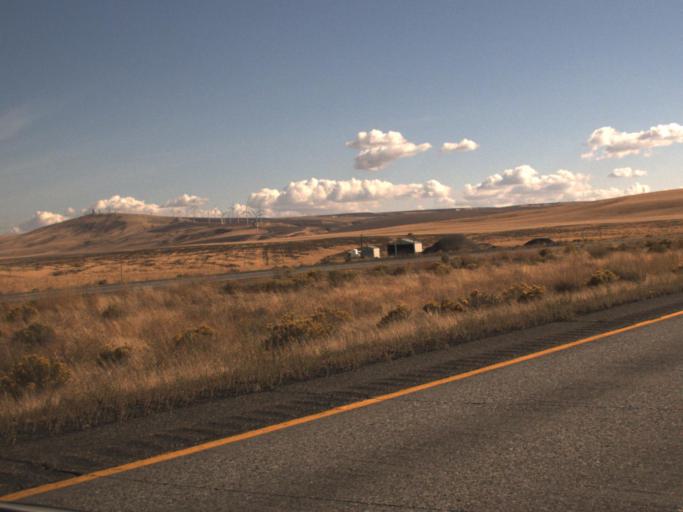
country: US
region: Washington
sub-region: Benton County
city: Highland
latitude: 46.1459
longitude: -119.2022
